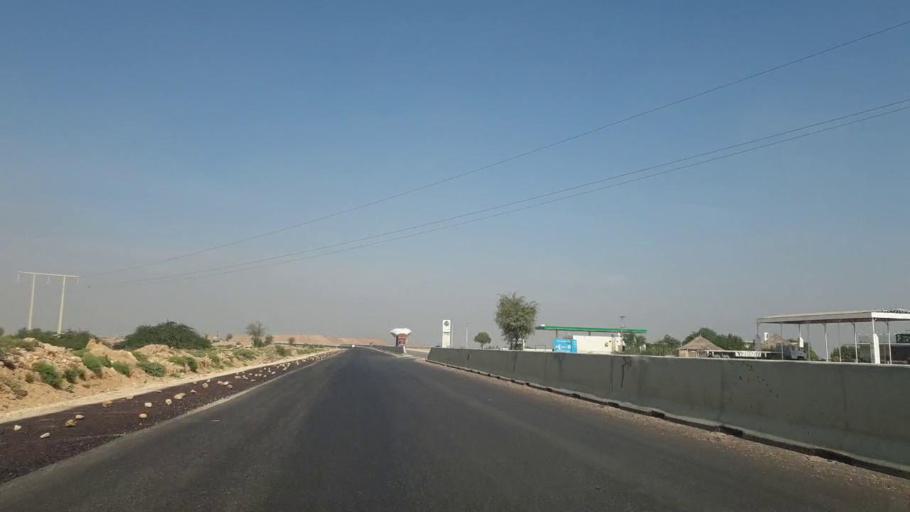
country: PK
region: Sindh
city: Jamshoro
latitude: 25.5698
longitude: 68.3135
